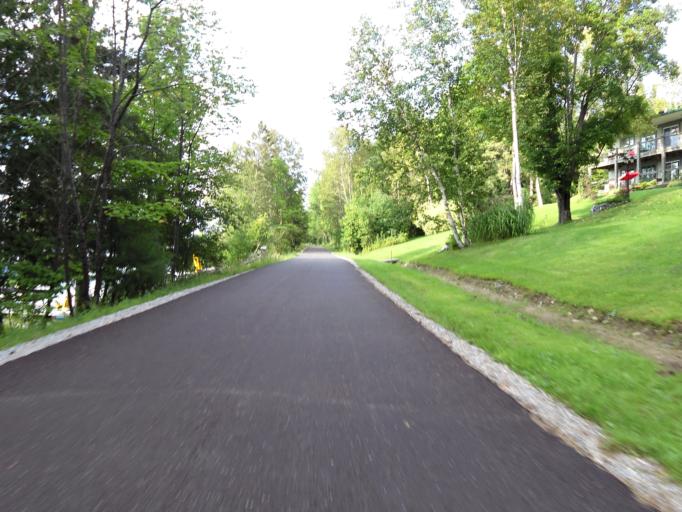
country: CA
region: Quebec
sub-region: Outaouais
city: Maniwaki
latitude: 46.2004
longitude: -76.0469
